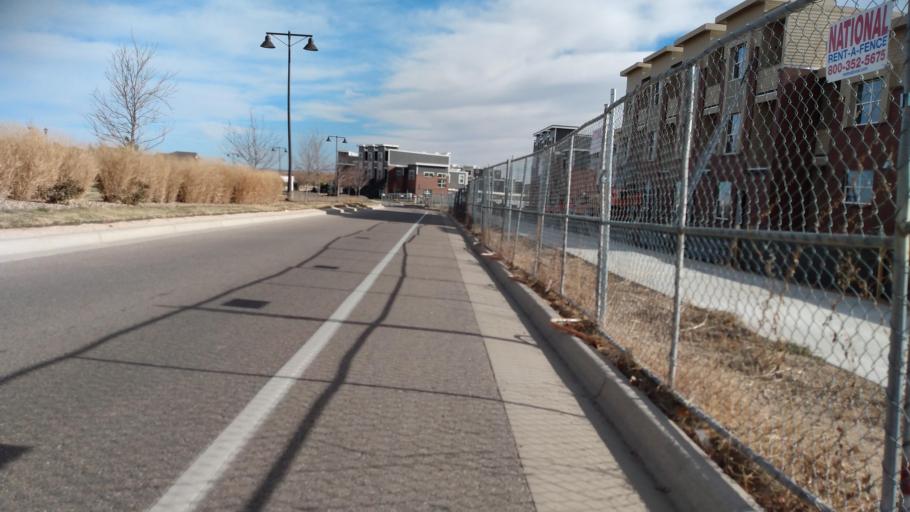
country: US
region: Colorado
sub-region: Boulder County
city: Erie
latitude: 40.0039
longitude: -104.9973
